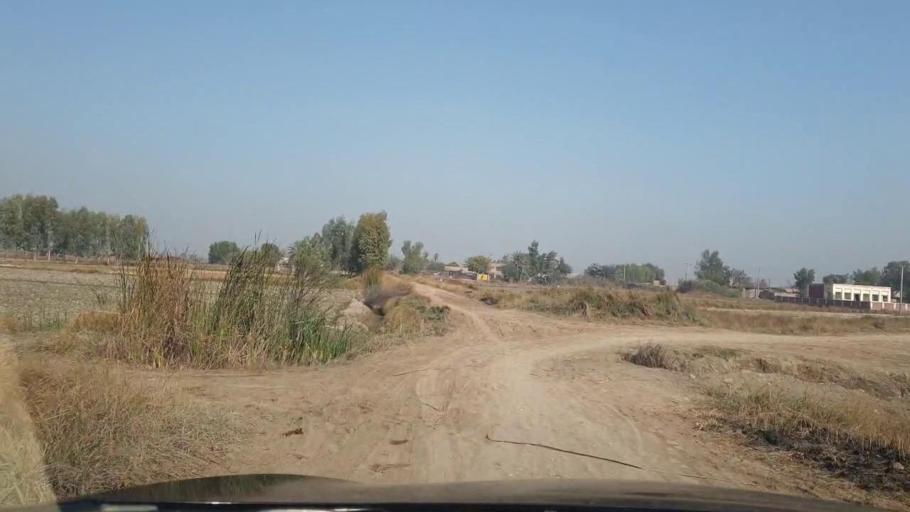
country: PK
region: Sindh
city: Ubauro
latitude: 28.1489
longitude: 69.7573
